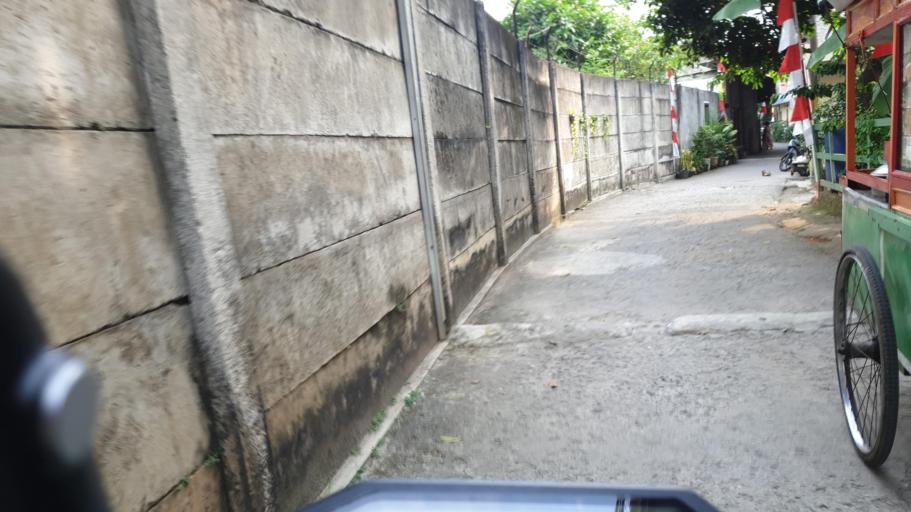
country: ID
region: West Java
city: Depok
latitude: -6.3407
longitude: 106.8296
